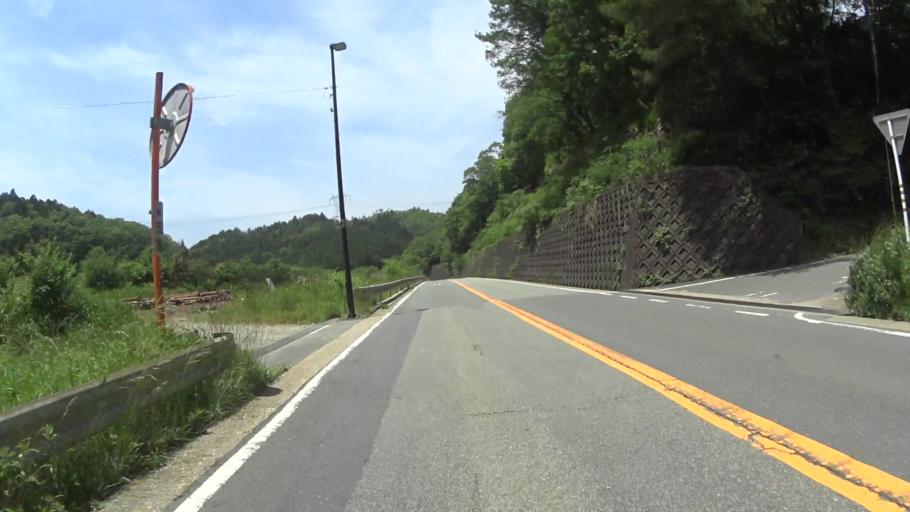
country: JP
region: Kyoto
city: Ayabe
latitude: 35.1879
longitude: 135.3365
